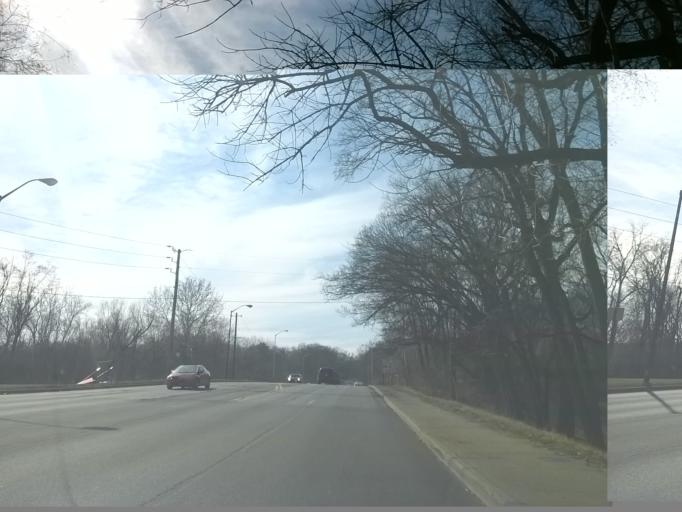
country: US
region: Indiana
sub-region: Marion County
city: Broad Ripple
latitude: 39.8622
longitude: -86.1599
